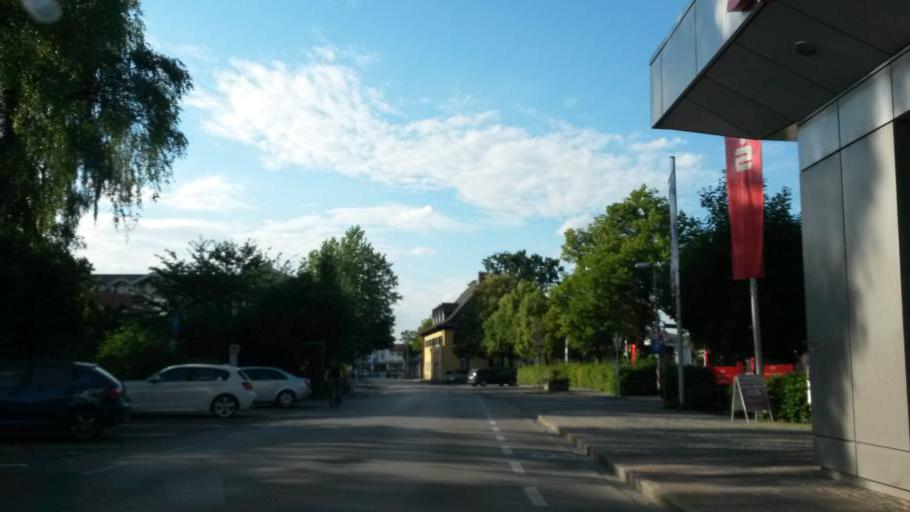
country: DE
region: Bavaria
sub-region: Upper Bavaria
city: Prien am Chiemsee
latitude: 47.8538
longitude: 12.3467
